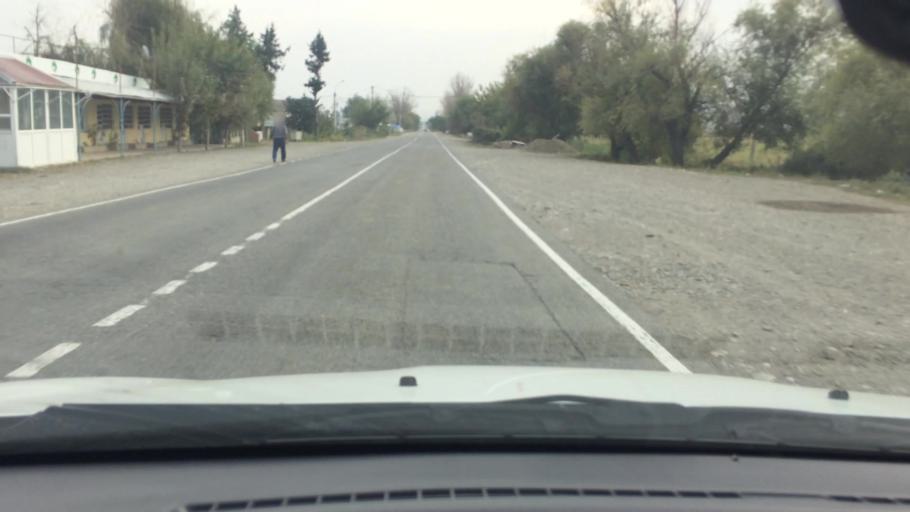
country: GE
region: Kvemo Kartli
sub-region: Gardabani
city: Gardabani
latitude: 41.4497
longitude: 44.9943
